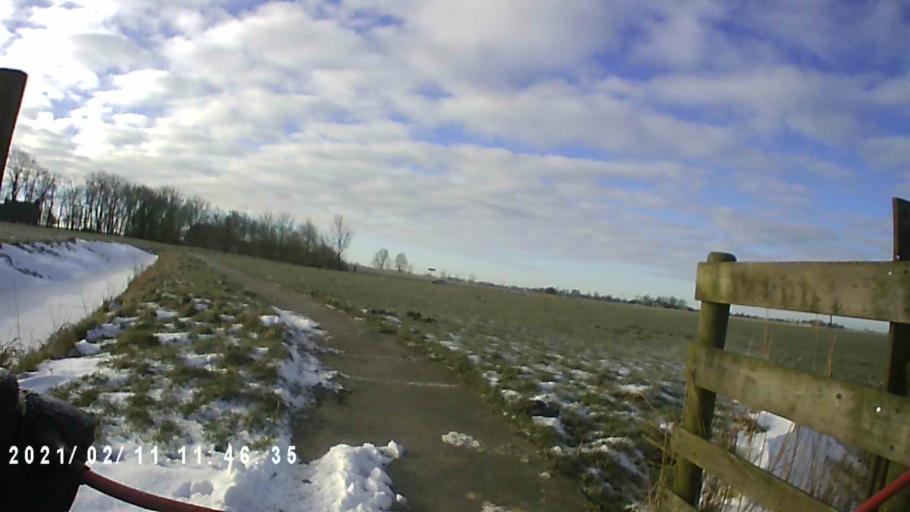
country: NL
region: Groningen
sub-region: Gemeente Zuidhorn
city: Aduard
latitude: 53.2806
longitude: 6.4489
